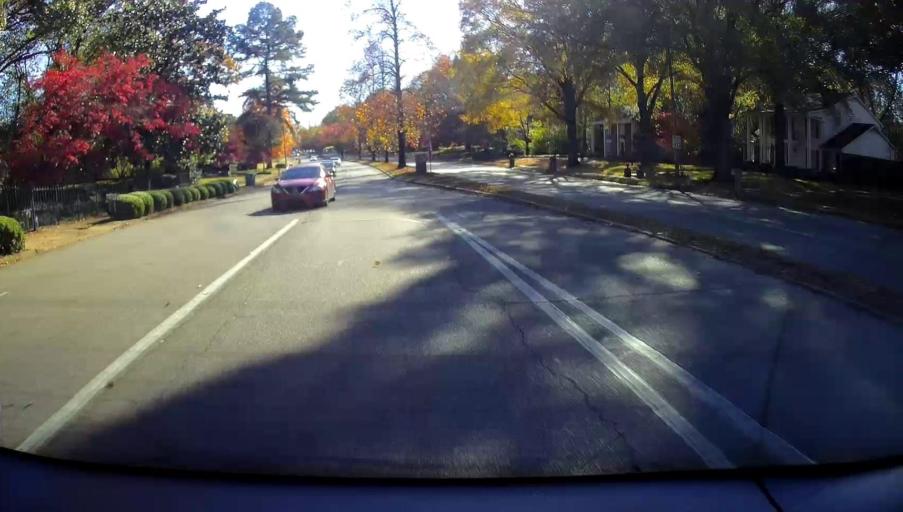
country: US
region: Tennessee
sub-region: Shelby County
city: Germantown
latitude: 35.0954
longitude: -89.8400
